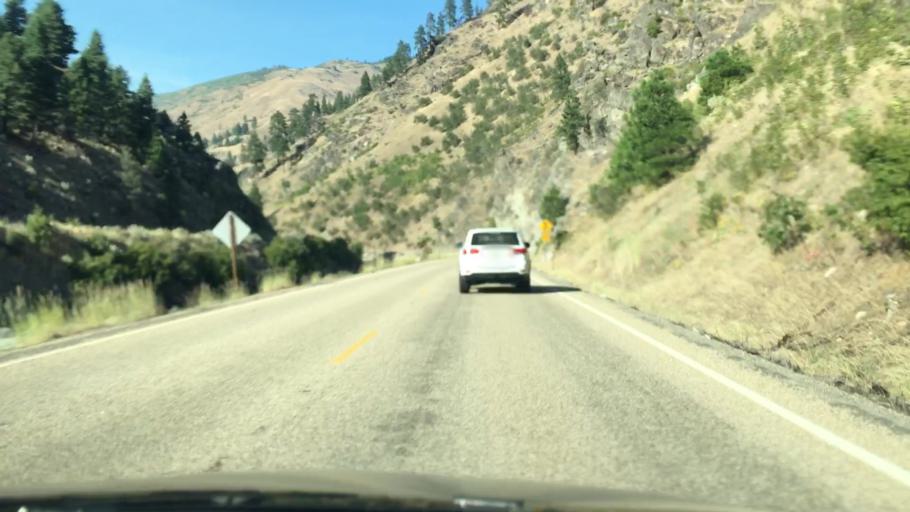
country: US
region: Idaho
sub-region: Boise County
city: Idaho City
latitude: 44.0902
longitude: -116.1053
